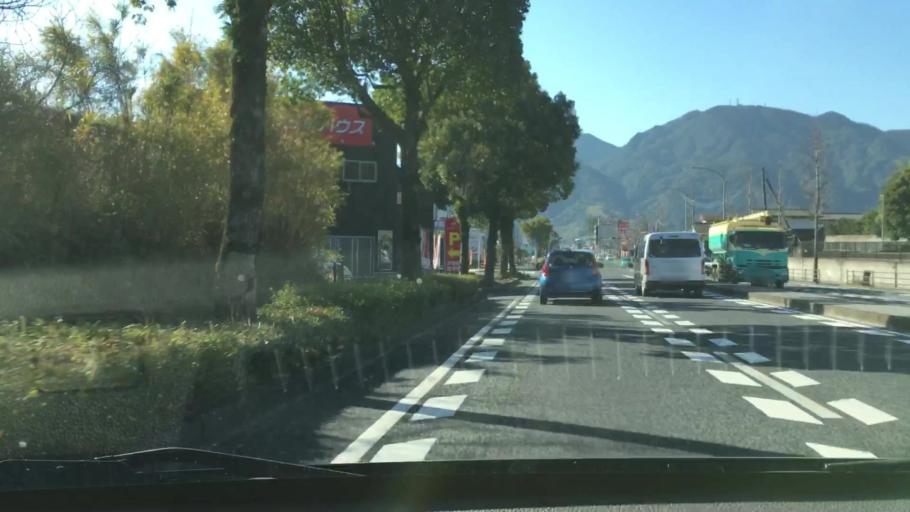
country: JP
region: Kagoshima
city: Kajiki
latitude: 31.7199
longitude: 130.6210
